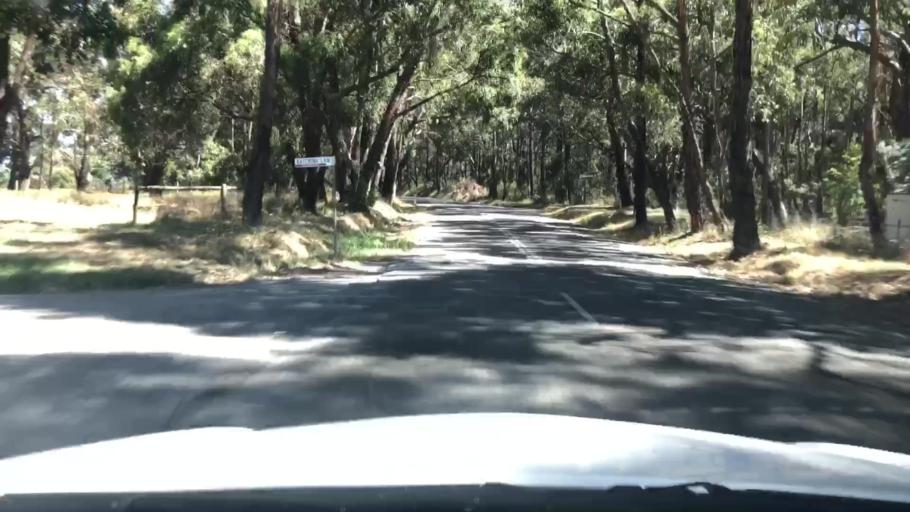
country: AU
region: Victoria
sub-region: Yarra Ranges
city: Macclesfield
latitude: -37.8763
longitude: 145.4779
